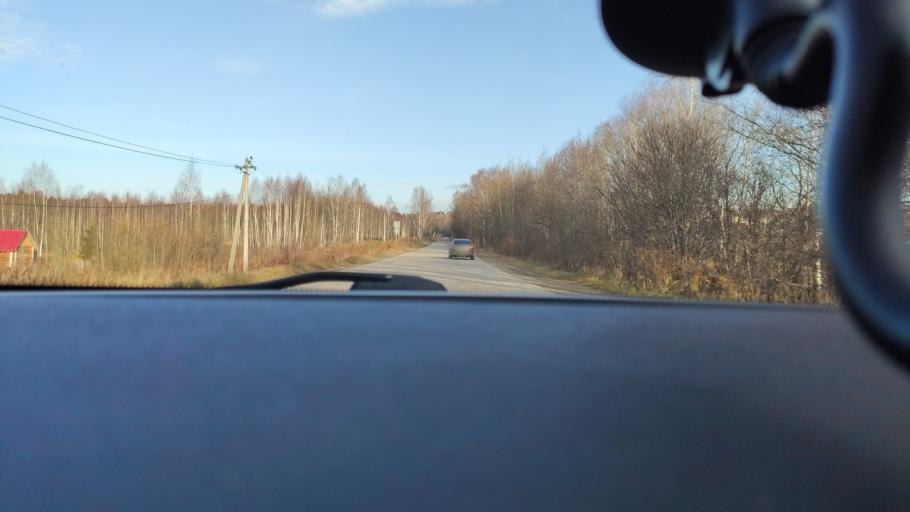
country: RU
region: Perm
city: Kondratovo
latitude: 58.0548
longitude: 56.0282
